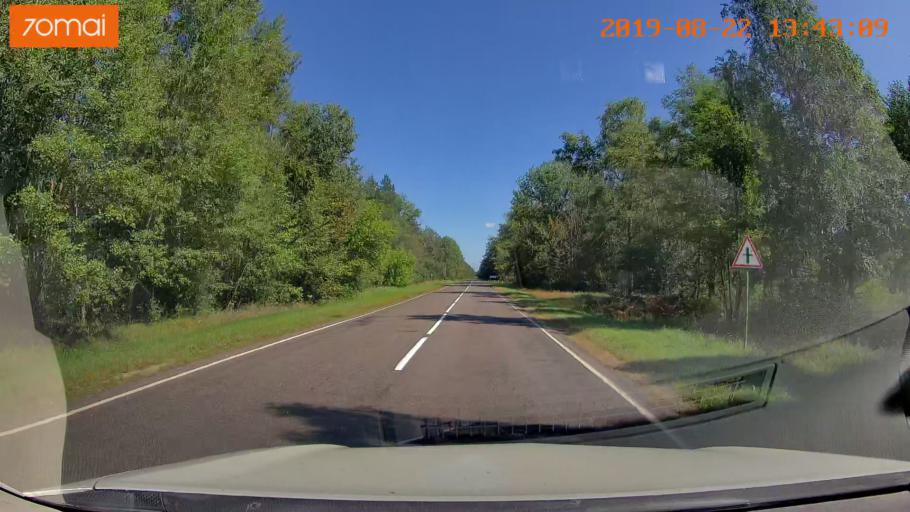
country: BY
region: Mogilev
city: Asipovichy
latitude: 53.2421
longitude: 28.4289
